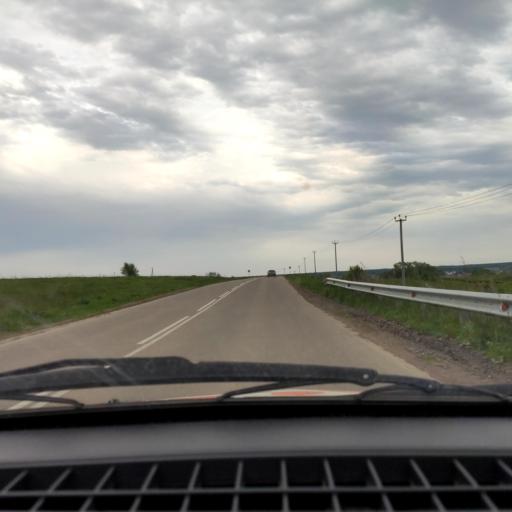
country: RU
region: Bashkortostan
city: Avdon
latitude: 54.5646
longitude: 55.7602
